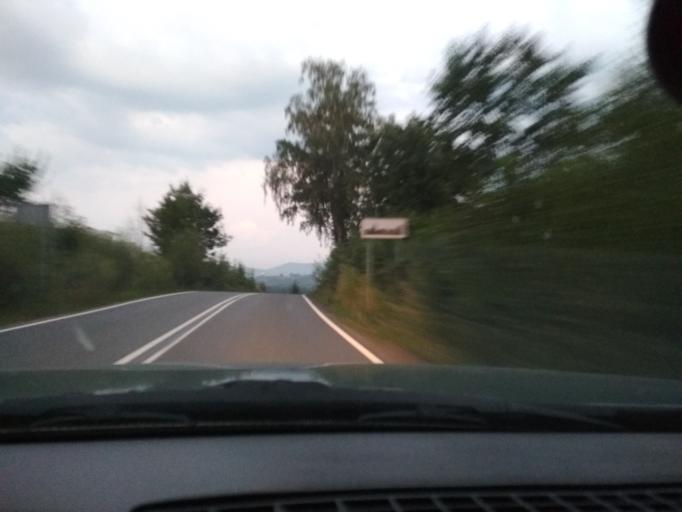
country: PL
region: Silesian Voivodeship
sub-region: Powiat bielski
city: Mazancowice
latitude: 49.8353
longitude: 18.9542
